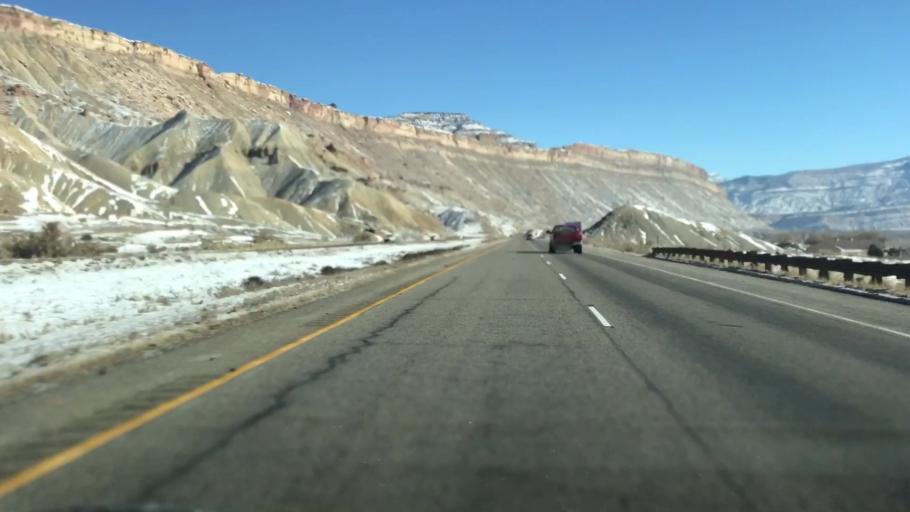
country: US
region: Colorado
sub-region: Mesa County
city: Palisade
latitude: 39.1158
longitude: -108.3964
